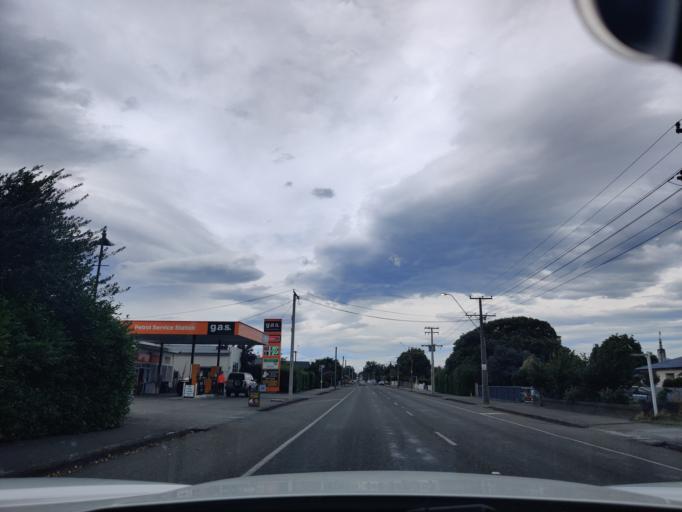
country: NZ
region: Wellington
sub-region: Masterton District
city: Masterton
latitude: -41.0332
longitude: 175.5195
